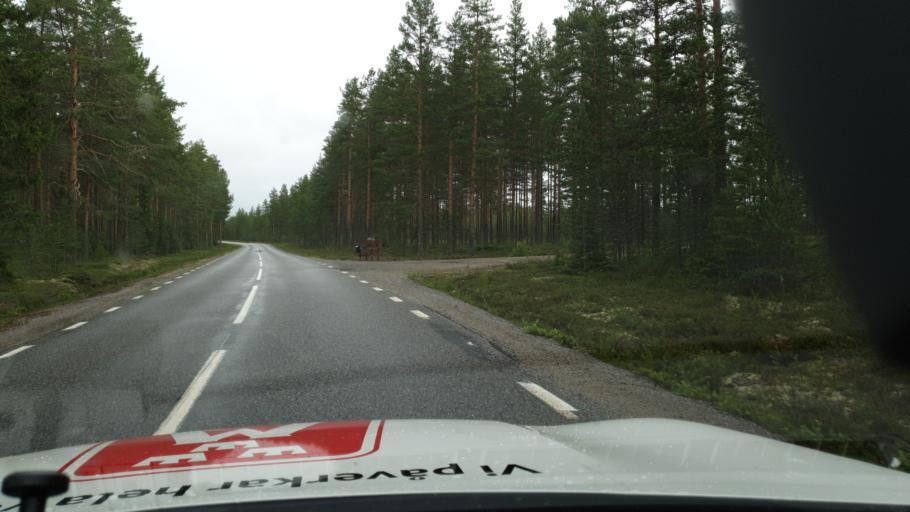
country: SE
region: Vaesterbotten
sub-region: Umea Kommun
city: Saevar
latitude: 63.9967
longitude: 20.4953
